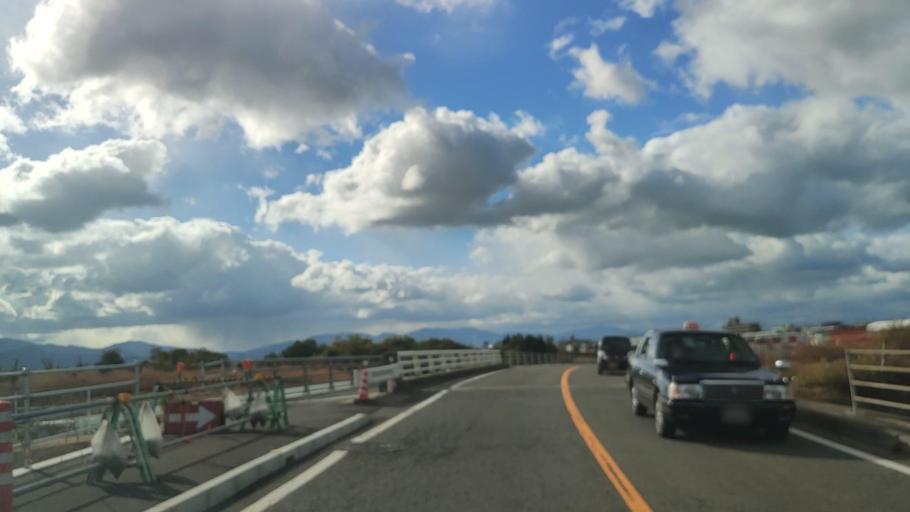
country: JP
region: Ehime
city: Masaki-cho
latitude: 33.8195
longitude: 132.7131
